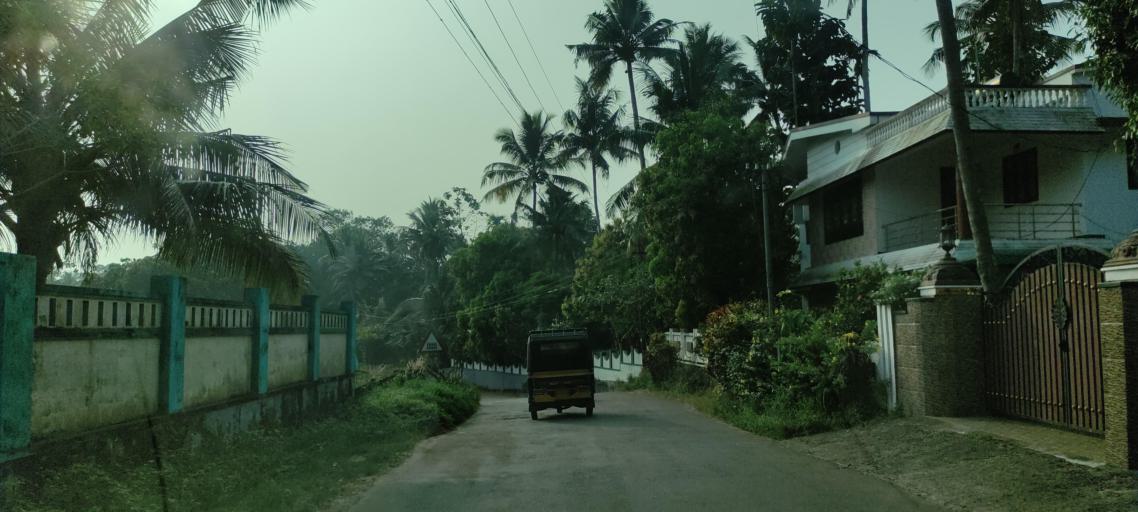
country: IN
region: Kerala
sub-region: Kottayam
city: Vaikam
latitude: 9.7568
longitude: 76.4943
